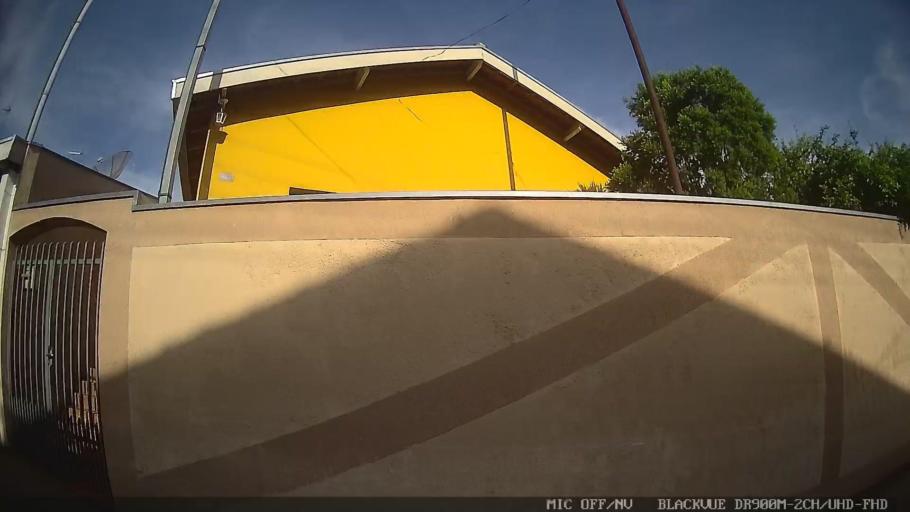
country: BR
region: Sao Paulo
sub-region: Tiete
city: Tiete
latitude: -23.0934
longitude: -47.7180
